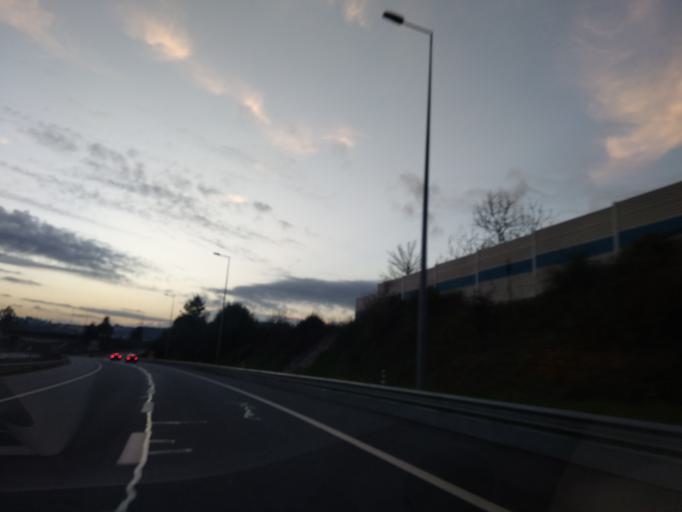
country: PT
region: Braga
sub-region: Vila Nova de Famalicao
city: Vila Nova de Famalicao
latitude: 41.3855
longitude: -8.5147
